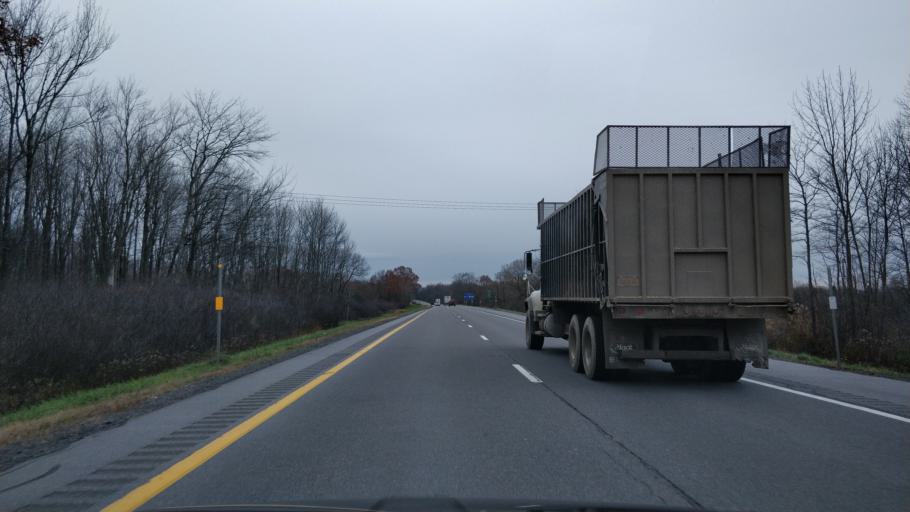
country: US
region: New York
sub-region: Oswego County
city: Pulaski
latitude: 43.6116
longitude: -76.0910
